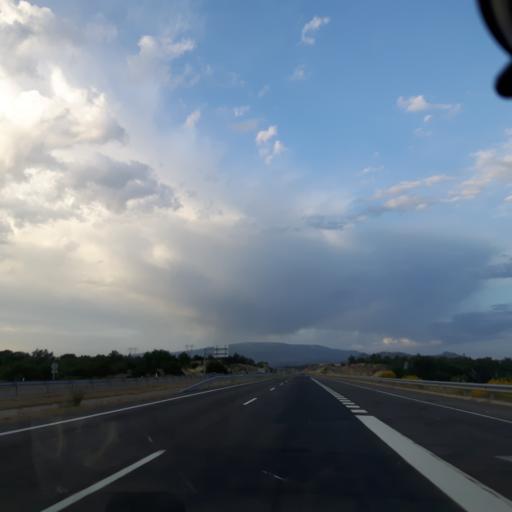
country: ES
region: Castille and Leon
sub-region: Provincia de Salamanca
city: Fuentes de Bejar
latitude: 40.5209
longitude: -5.6724
